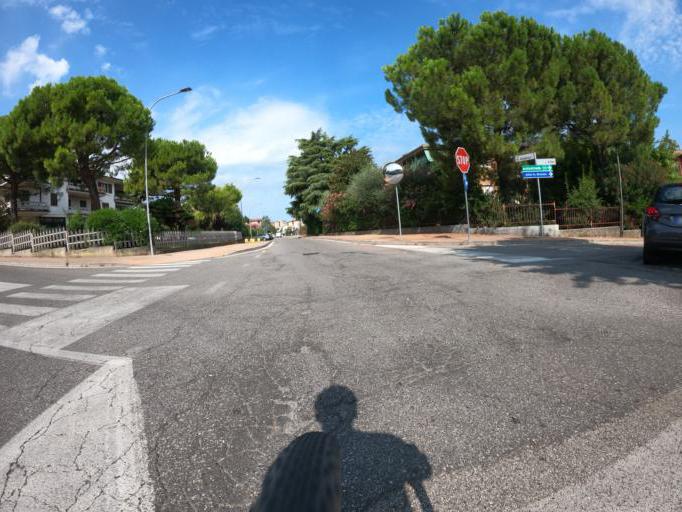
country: IT
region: Lombardy
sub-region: Provincia di Brescia
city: Desenzano del Garda
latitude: 45.4640
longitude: 10.5432
